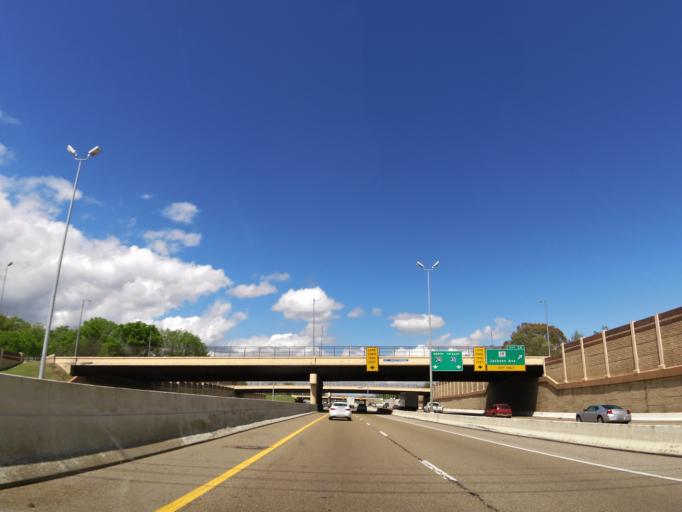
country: US
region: Tennessee
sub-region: Shelby County
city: Memphis
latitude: 35.1534
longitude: -90.0212
